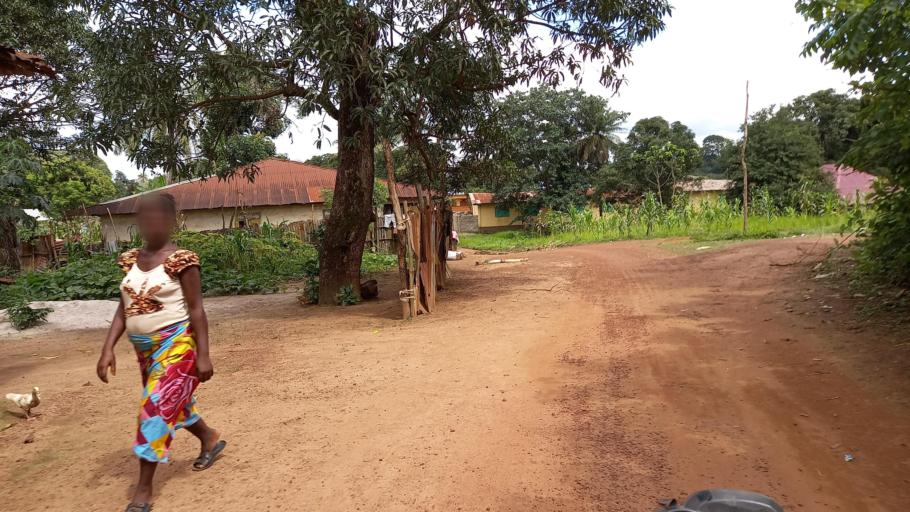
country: SL
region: Northern Province
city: Kamakwie
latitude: 9.5043
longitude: -12.2406
